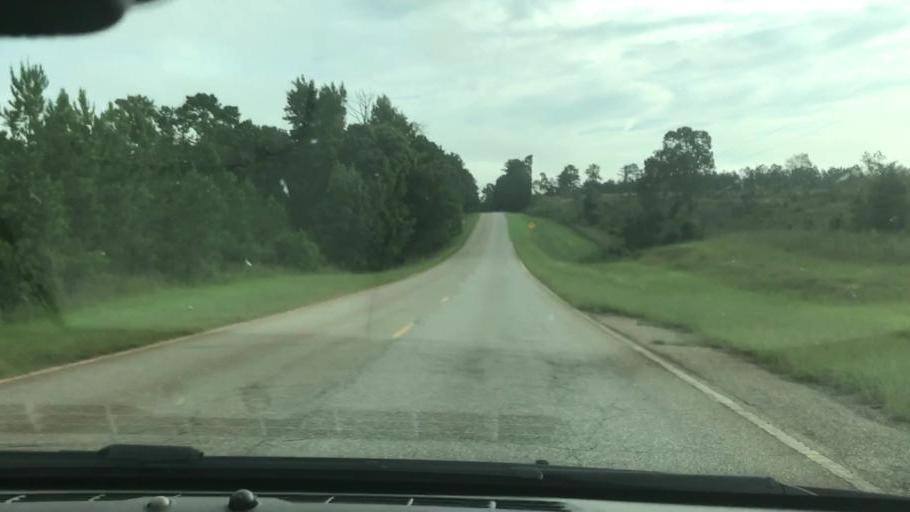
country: US
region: Georgia
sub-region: Quitman County
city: Georgetown
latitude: 31.9219
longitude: -85.0216
